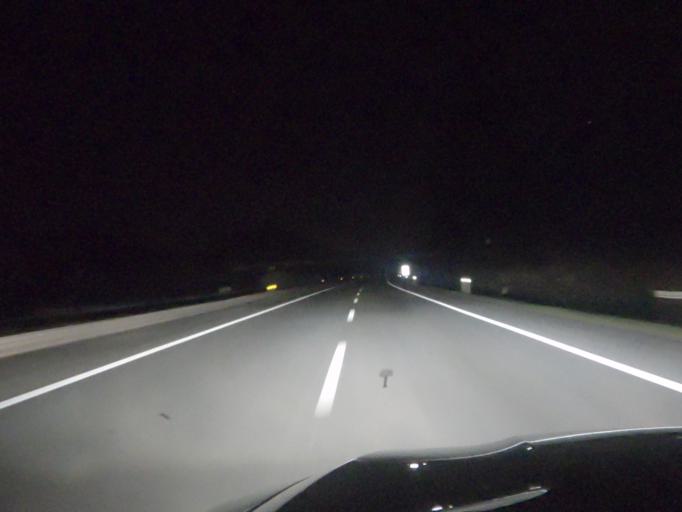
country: PT
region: Aveiro
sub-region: Estarreja
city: Salreu
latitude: 40.7160
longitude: -8.5221
